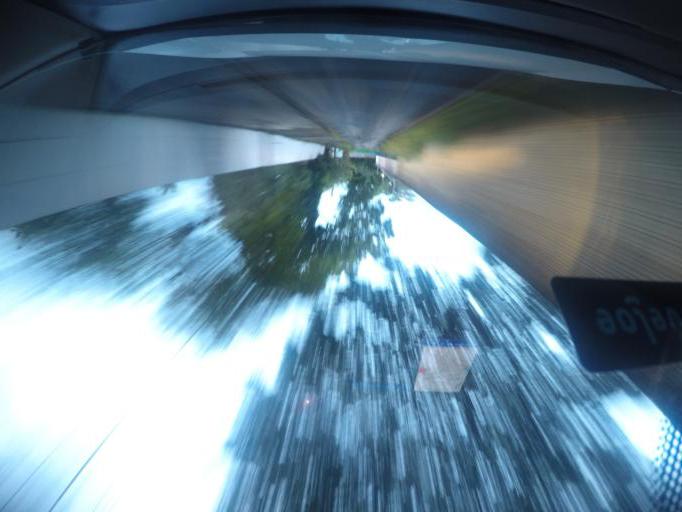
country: BR
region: Goias
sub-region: Goiania
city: Goiania
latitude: -16.6424
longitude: -49.2449
